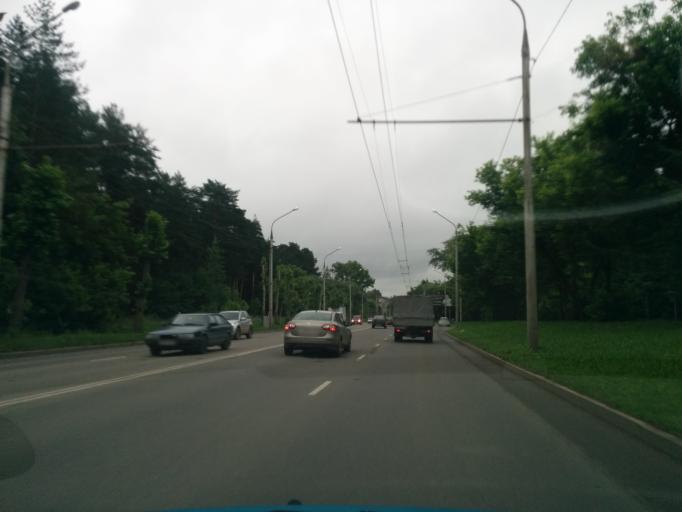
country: RU
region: Perm
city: Perm
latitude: 57.9912
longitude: 56.1845
